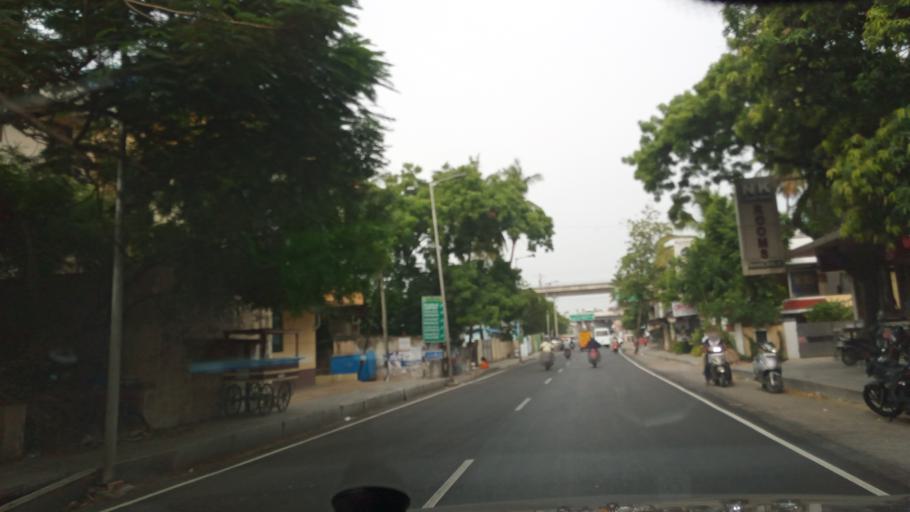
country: IN
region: Tamil Nadu
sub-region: Kancheepuram
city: Saint Thomas Mount
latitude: 13.0086
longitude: 80.2009
